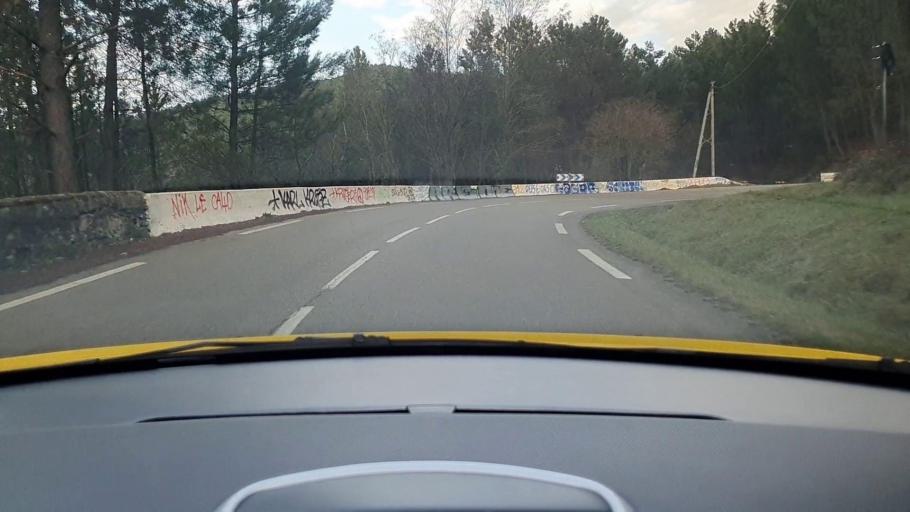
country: FR
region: Languedoc-Roussillon
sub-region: Departement du Gard
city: Les Salles-du-Gardon
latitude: 44.2542
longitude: 4.0447
